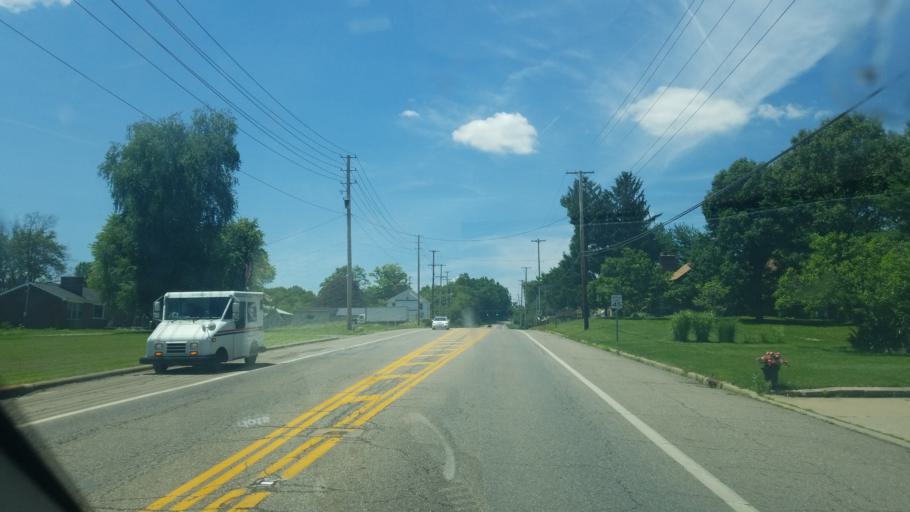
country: US
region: Ohio
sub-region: Columbiana County
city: Salem
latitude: 40.8790
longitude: -80.8546
